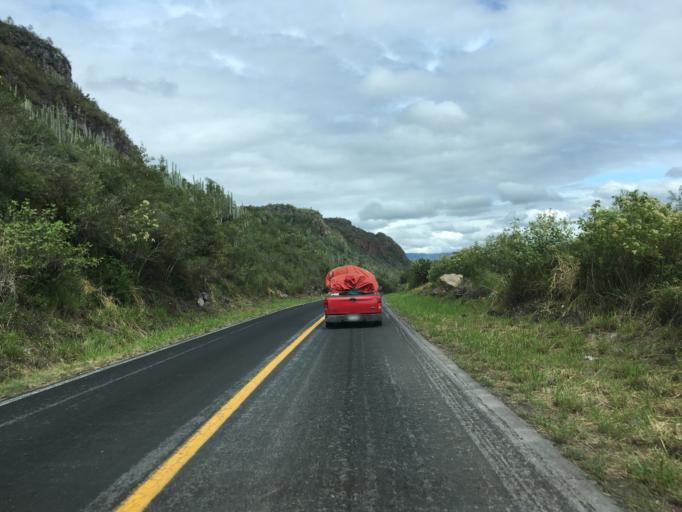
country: MX
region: Hidalgo
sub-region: Atotonilco el Grande
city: Santa Maria Amajac
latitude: 20.4229
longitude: -98.6874
